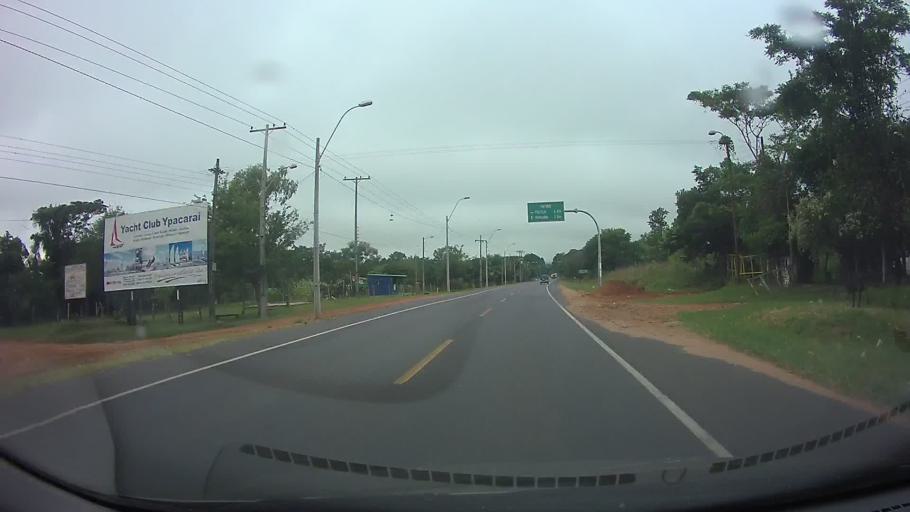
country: PY
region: Central
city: Itaugua
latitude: -25.3474
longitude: -57.3388
